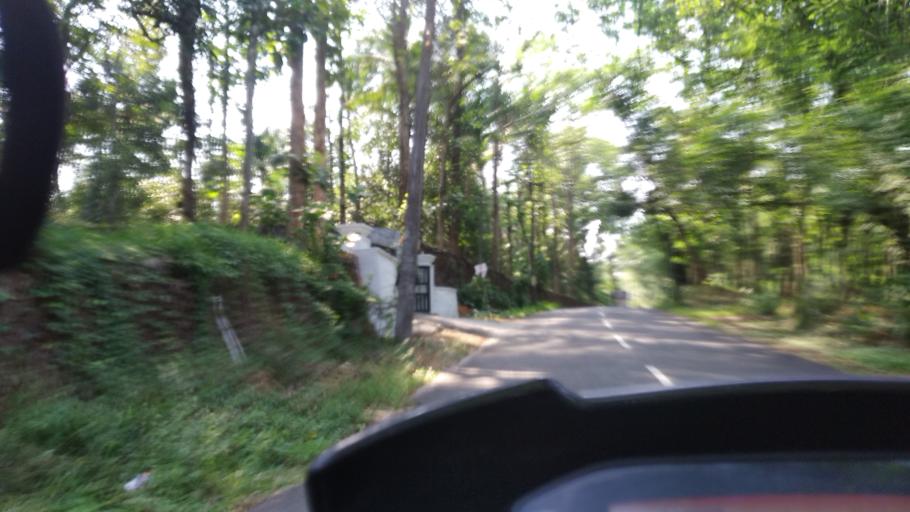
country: IN
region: Kerala
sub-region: Kottayam
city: Palackattumala
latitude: 9.8038
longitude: 76.5760
